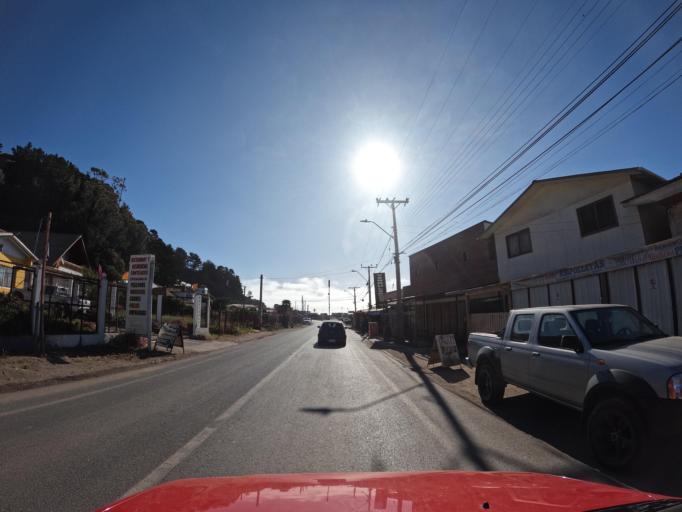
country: CL
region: Maule
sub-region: Provincia de Talca
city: Constitucion
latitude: -34.8851
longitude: -72.1624
